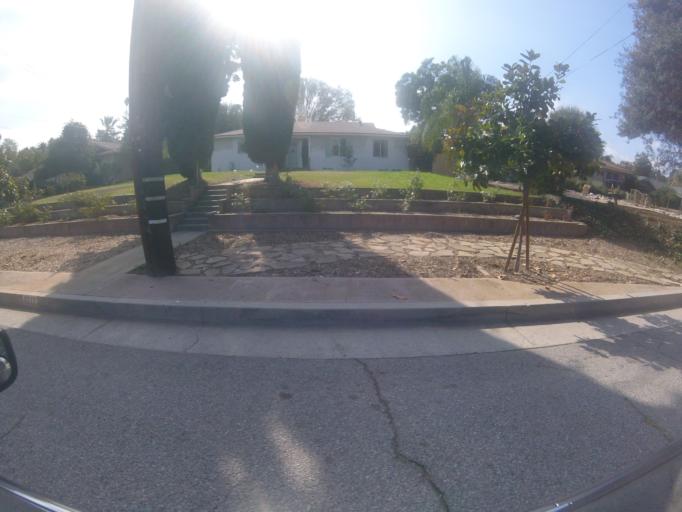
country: US
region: California
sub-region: San Bernardino County
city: Redlands
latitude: 34.0319
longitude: -117.1870
